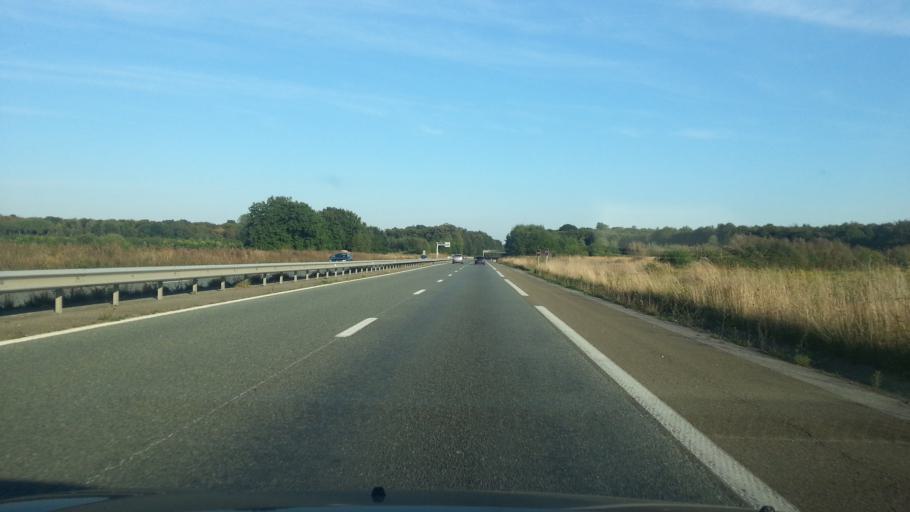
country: FR
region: Picardie
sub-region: Departement de l'Oise
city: Agnetz
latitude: 49.4098
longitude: 2.3388
